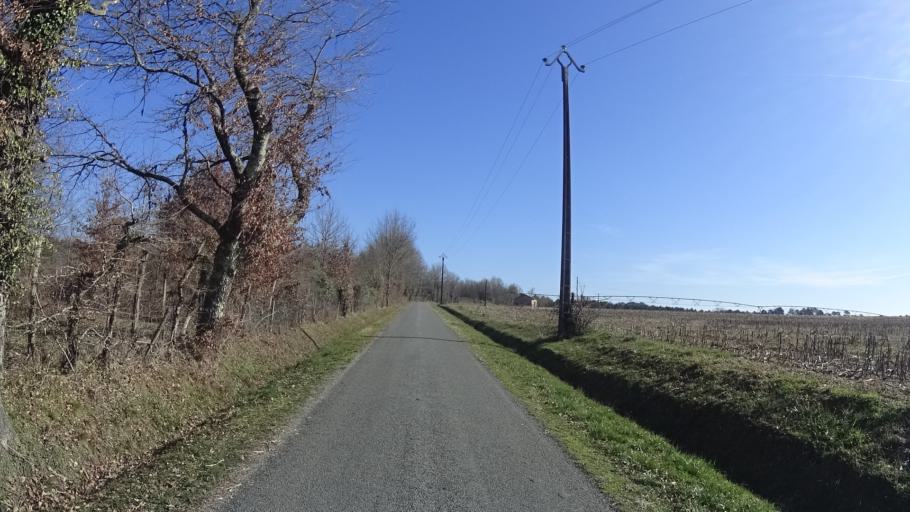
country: FR
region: Aquitaine
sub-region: Departement de la Dordogne
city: Montpon-Menesterol
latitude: 45.1017
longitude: 0.1992
